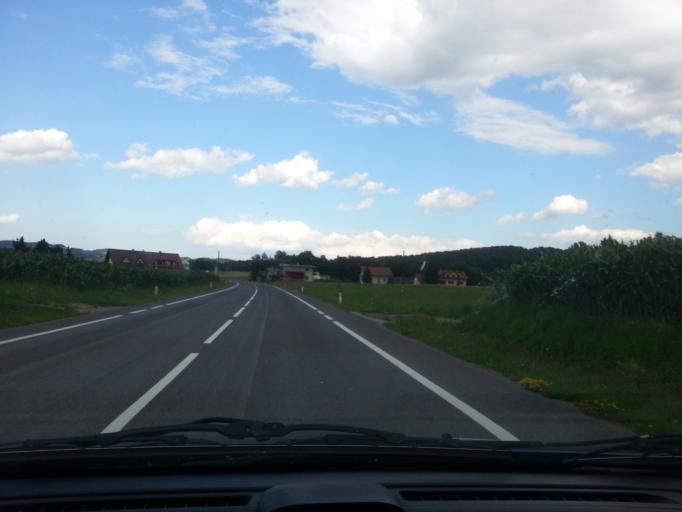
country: AT
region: Styria
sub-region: Politischer Bezirk Leibnitz
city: Oberhaag
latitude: 46.6853
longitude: 15.3544
